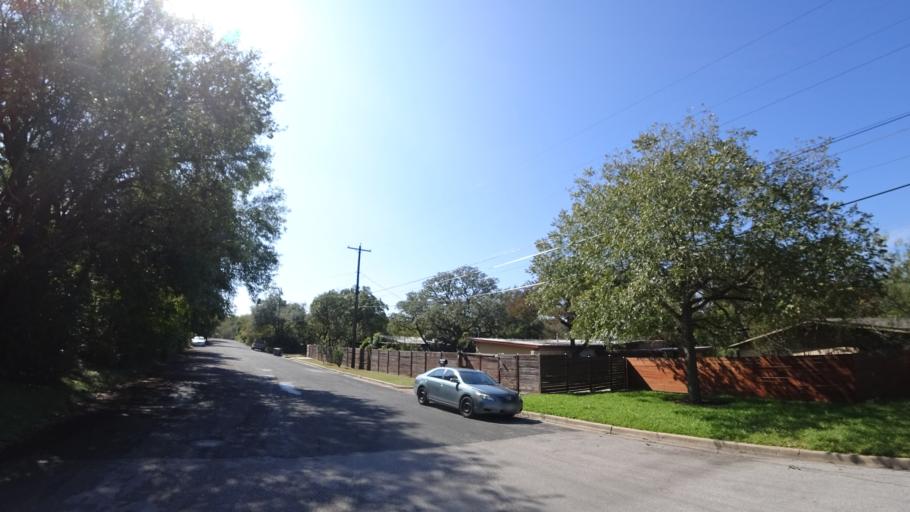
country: US
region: Texas
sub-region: Travis County
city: Austin
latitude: 30.2593
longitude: -97.7696
